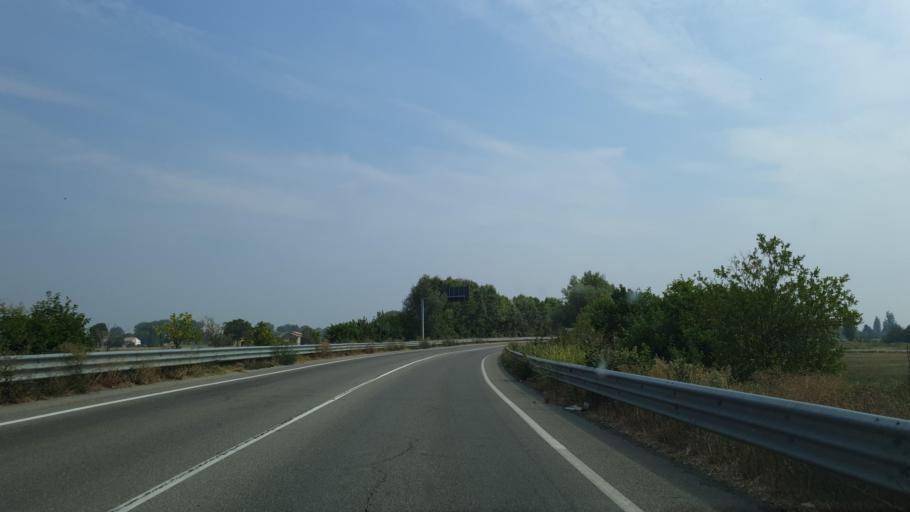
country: IT
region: Emilia-Romagna
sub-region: Provincia di Parma
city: San Secondo Parmense
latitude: 44.9282
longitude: 10.2393
